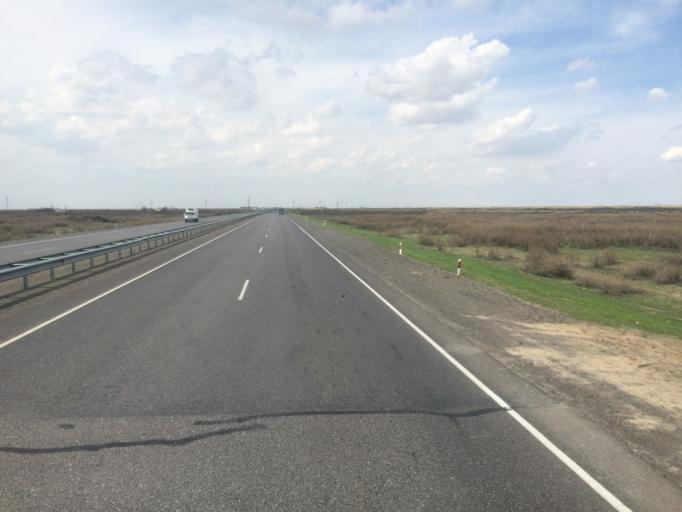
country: KZ
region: Qyzylorda
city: Zhangaqorghan
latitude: 43.9954
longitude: 67.2264
